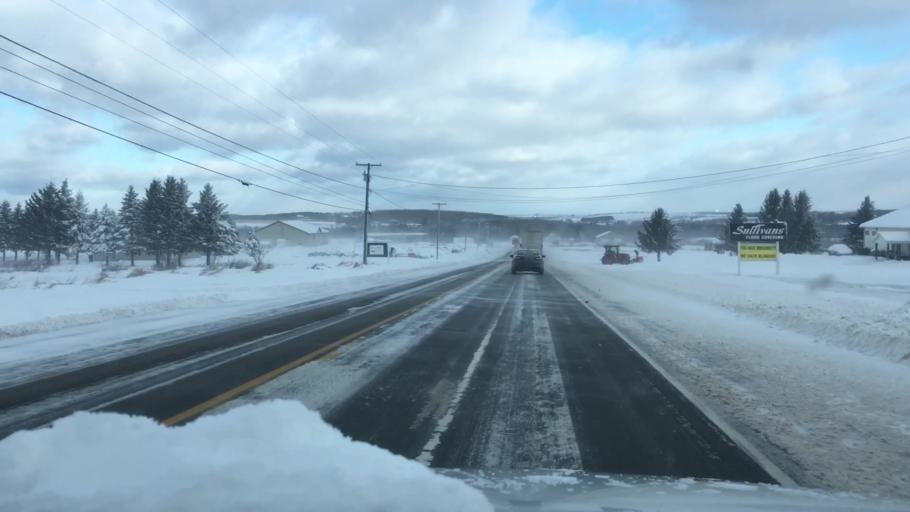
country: US
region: Maine
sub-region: Aroostook County
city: Caribou
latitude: 46.7948
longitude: -67.9914
